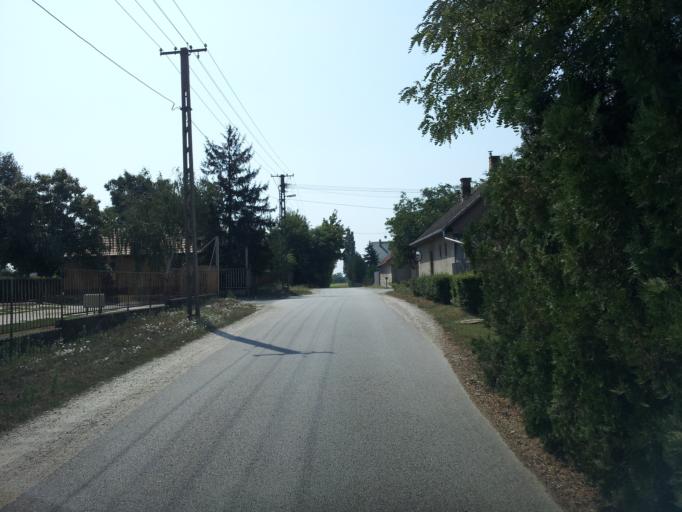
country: HU
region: Pest
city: Dunavarsany
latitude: 47.2880
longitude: 19.0360
